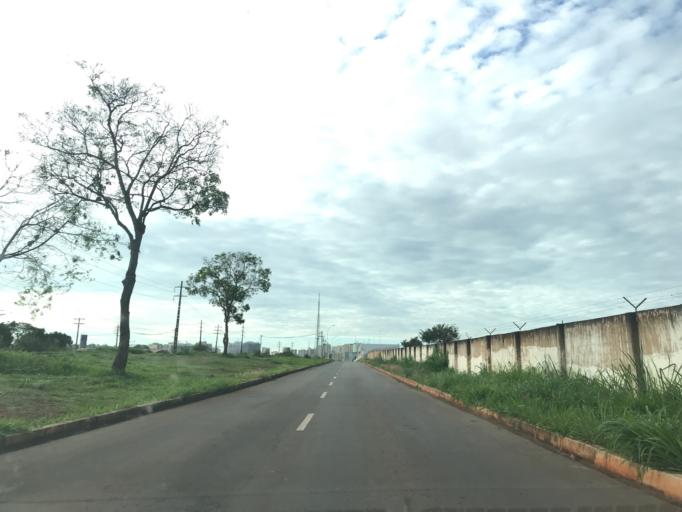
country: BR
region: Federal District
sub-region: Brasilia
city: Brasilia
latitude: -15.7742
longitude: -47.8955
